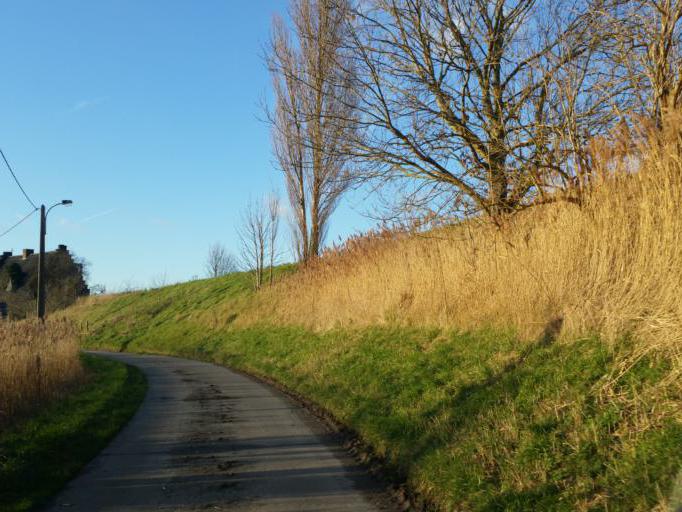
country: NL
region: North Brabant
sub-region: Gemeente Woensdrecht
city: Woensdrecht
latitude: 51.3363
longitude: 4.2464
